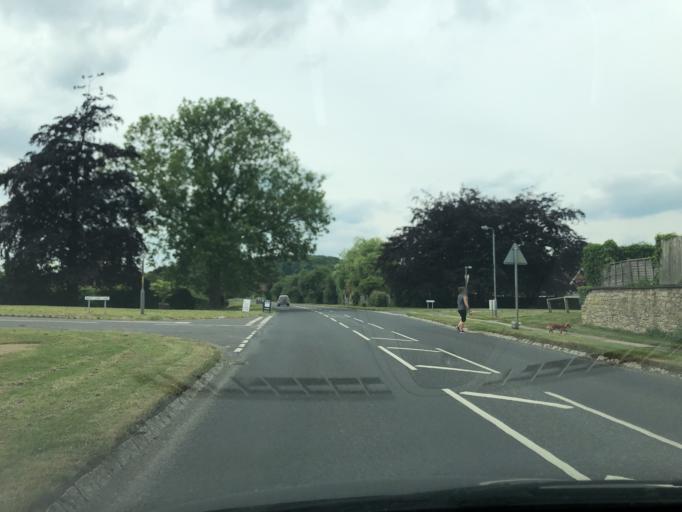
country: GB
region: England
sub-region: North Yorkshire
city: Helmsley
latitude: 54.2671
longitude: -0.9352
